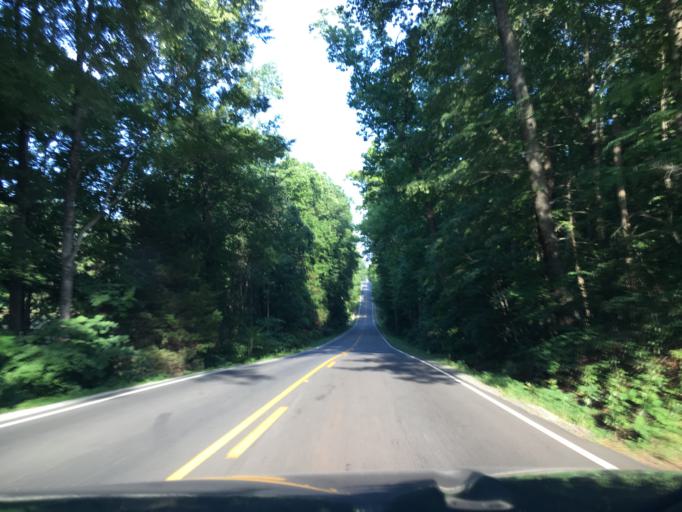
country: US
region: Virginia
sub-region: Franklin County
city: Union Hall
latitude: 36.9708
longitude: -79.6004
